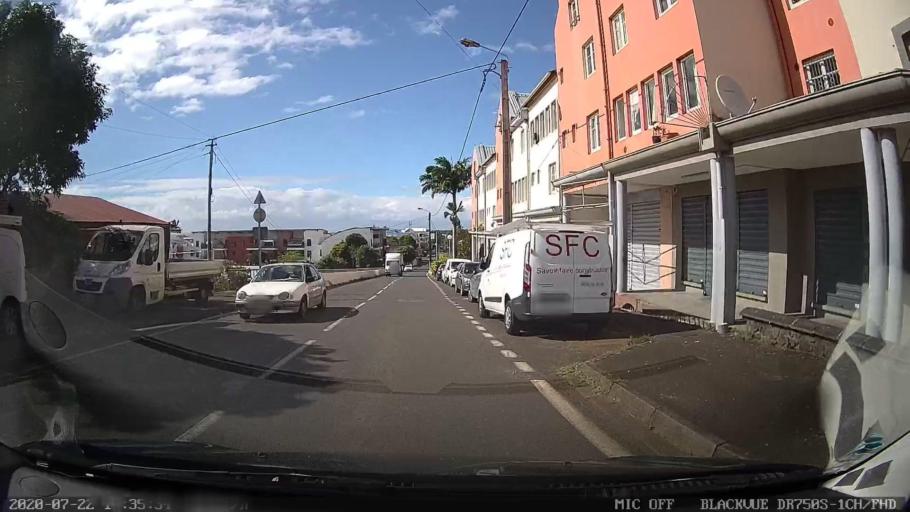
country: RE
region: Reunion
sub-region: Reunion
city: Sainte-Suzanne
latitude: -20.9042
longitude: 55.6038
